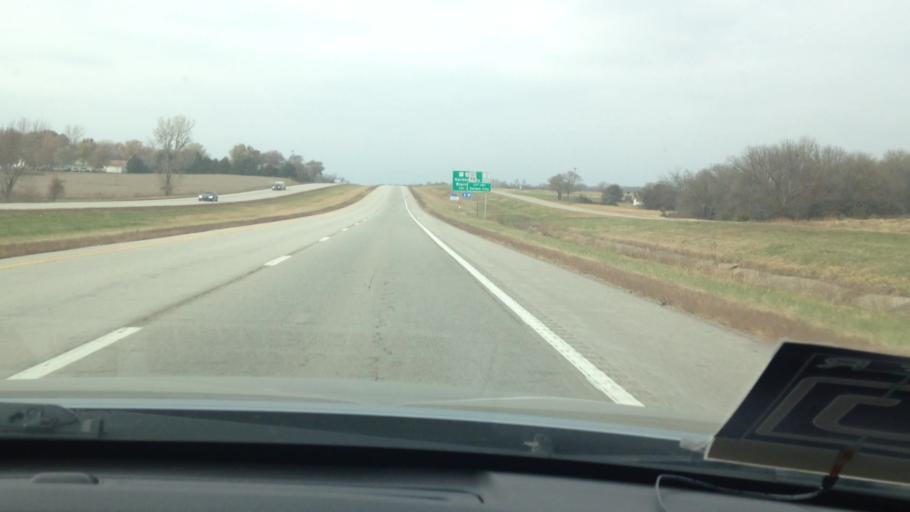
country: US
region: Missouri
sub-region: Cass County
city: Garden City
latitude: 38.5587
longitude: -94.1812
